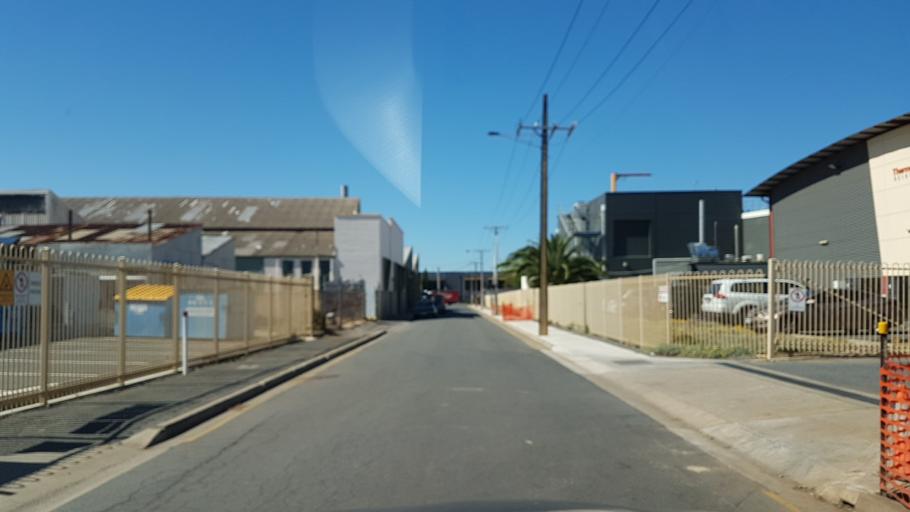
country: AU
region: South Australia
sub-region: City of West Torrens
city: Thebarton
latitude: -34.9120
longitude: 138.5714
